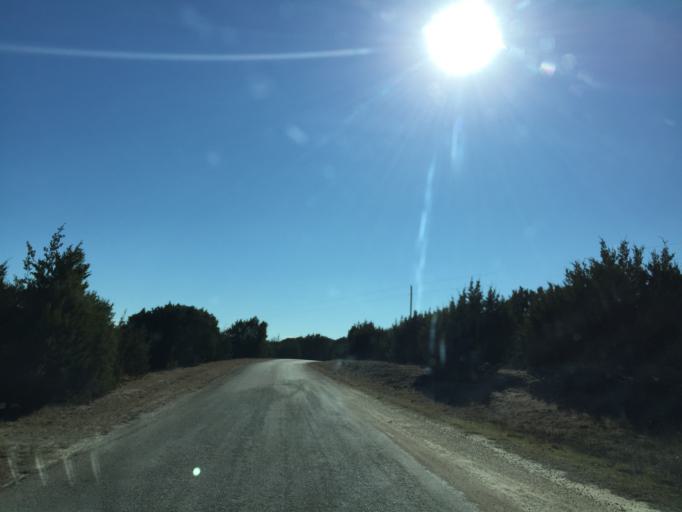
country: US
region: Texas
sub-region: Lampasas County
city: Lampasas
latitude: 30.9435
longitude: -98.1654
